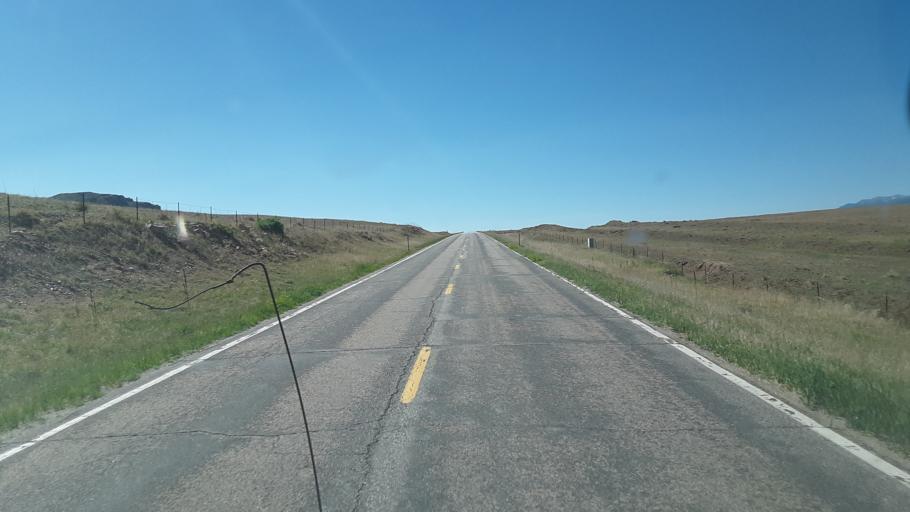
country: US
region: Colorado
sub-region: Custer County
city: Westcliffe
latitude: 38.2086
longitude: -105.5430
